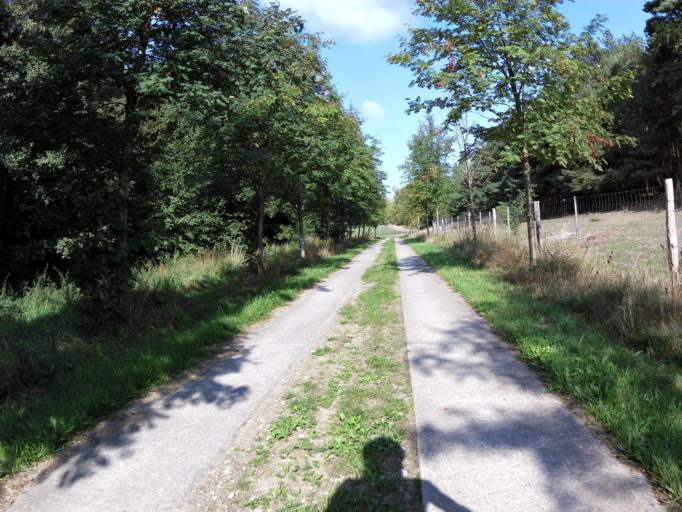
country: DE
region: Mecklenburg-Vorpommern
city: Loddin
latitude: 53.9507
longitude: 14.0405
